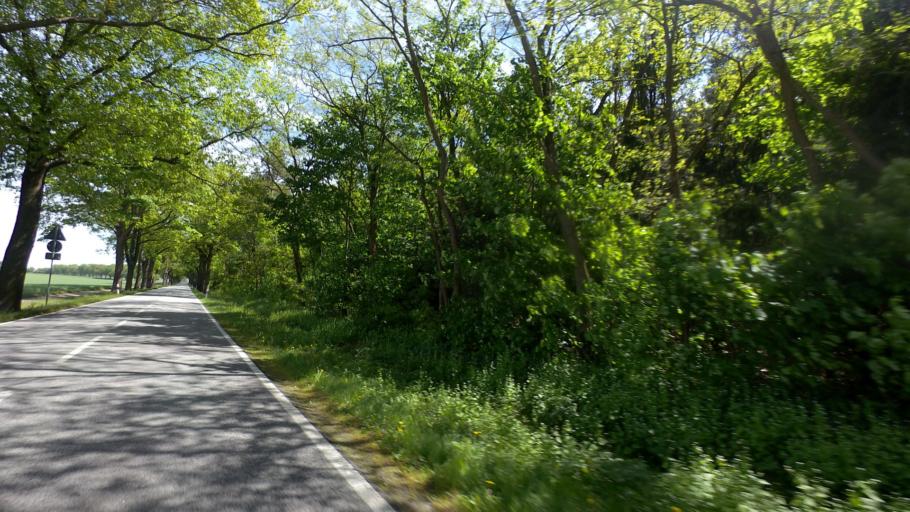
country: DE
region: Brandenburg
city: Baruth
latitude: 52.0480
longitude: 13.4520
